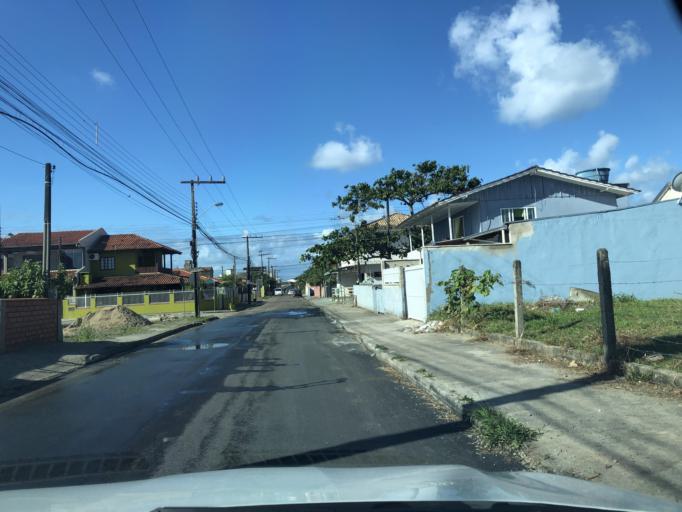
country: BR
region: Santa Catarina
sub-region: Sao Francisco Do Sul
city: Sao Francisco do Sul
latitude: -26.2322
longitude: -48.5053
